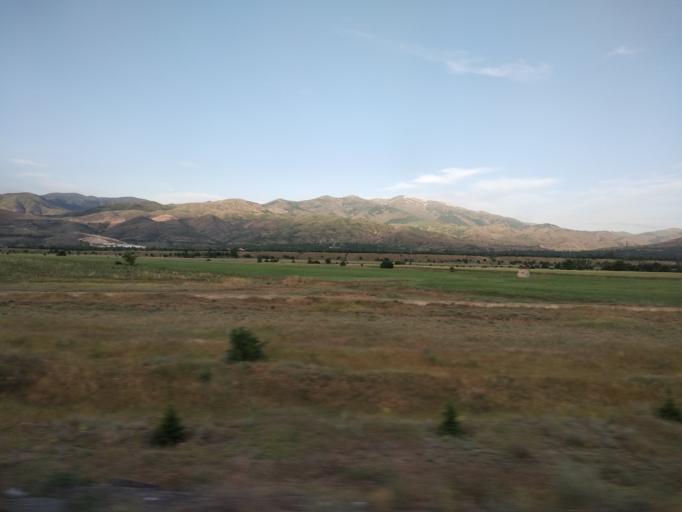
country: TR
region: Erzincan
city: Catalarmut
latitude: 39.8152
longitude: 39.3547
